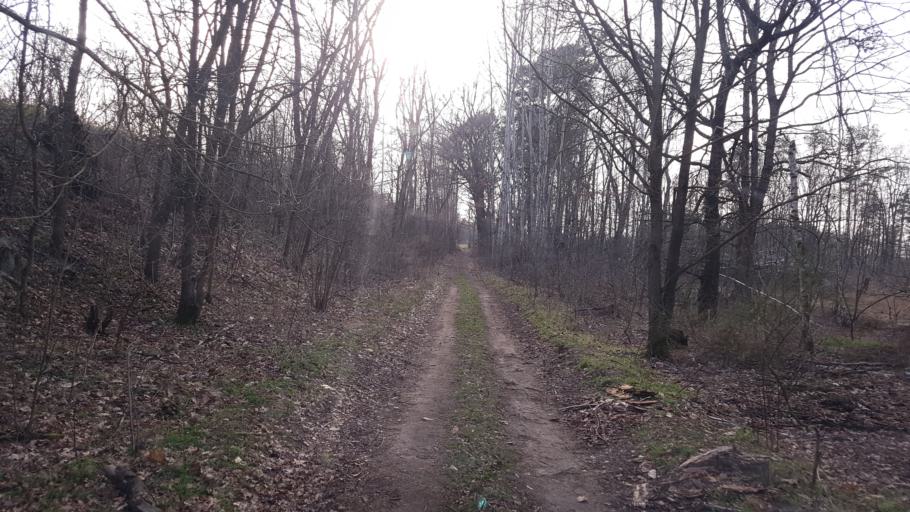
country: DE
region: Brandenburg
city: Doberlug-Kirchhain
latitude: 51.6269
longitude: 13.5947
